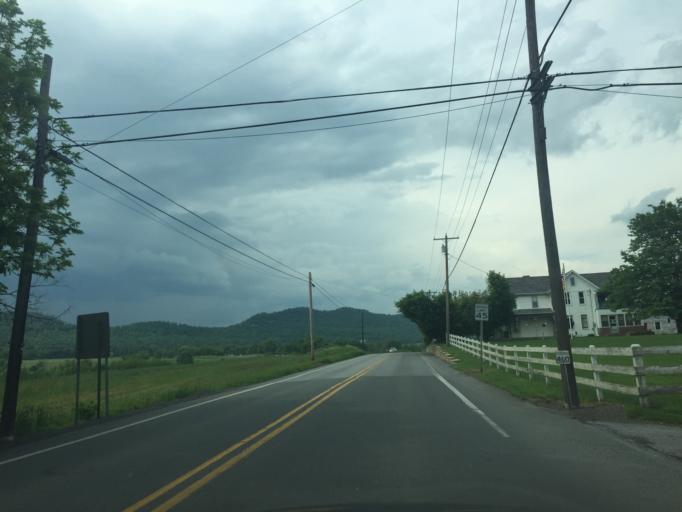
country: US
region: Pennsylvania
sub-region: Fulton County
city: McConnellsburg
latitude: 39.9372
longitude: -77.9969
